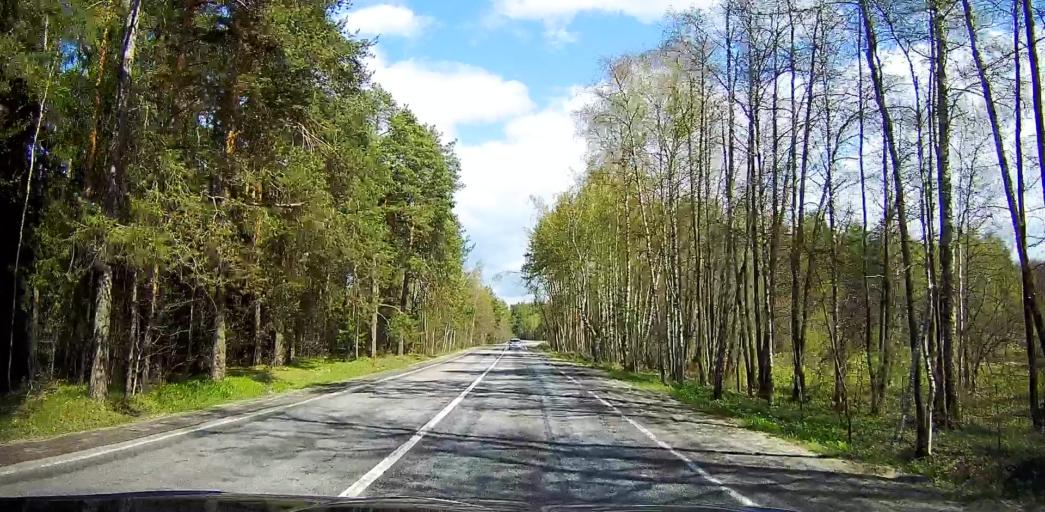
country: RU
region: Moskovskaya
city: Davydovo
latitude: 55.5626
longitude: 38.8544
